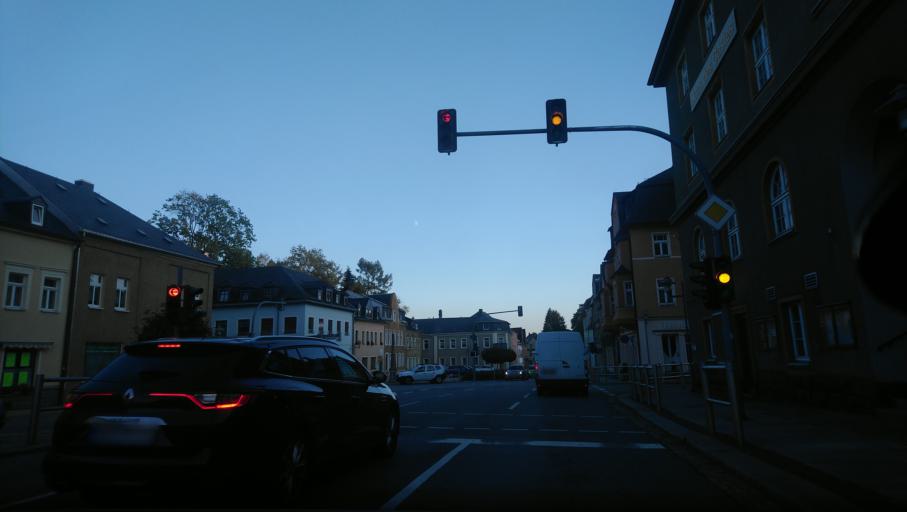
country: DE
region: Saxony
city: Geyer
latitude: 50.6239
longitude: 12.9233
